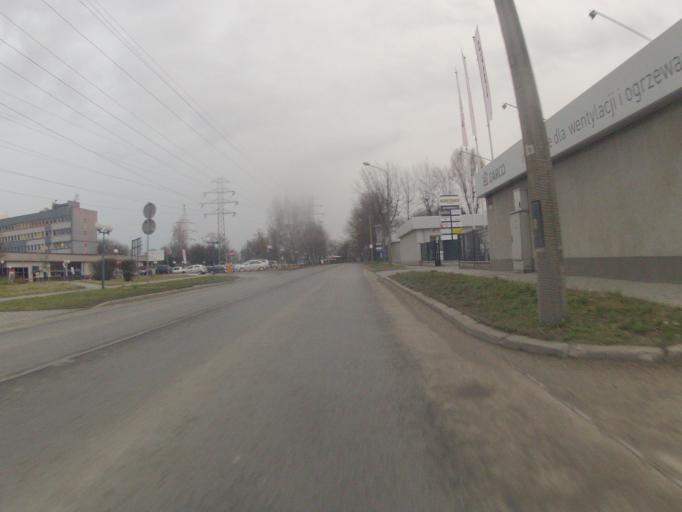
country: PL
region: Lesser Poland Voivodeship
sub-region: Krakow
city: Krakow
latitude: 50.0539
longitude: 20.0025
